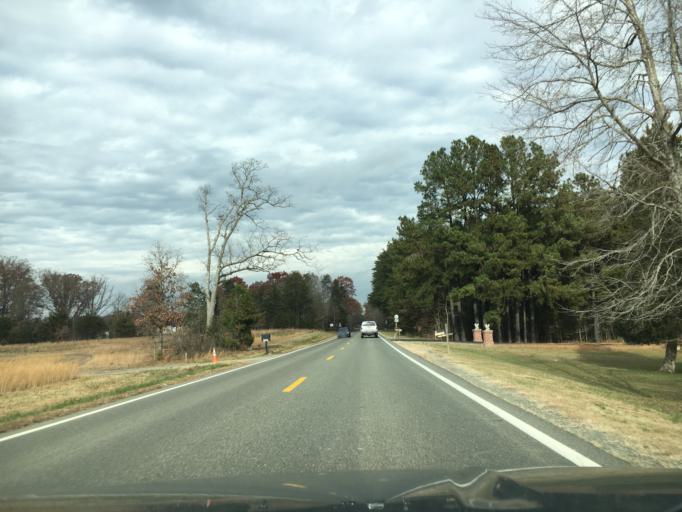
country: US
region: Virginia
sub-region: Prince Edward County
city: Farmville
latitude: 37.4123
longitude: -78.3552
